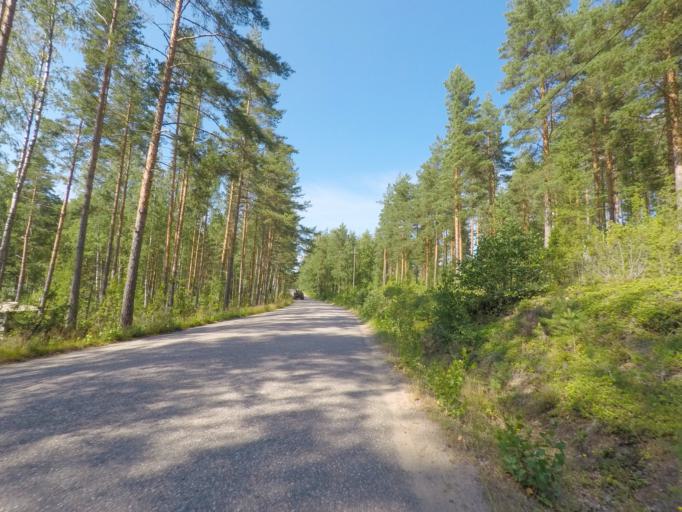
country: FI
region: Southern Savonia
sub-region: Mikkeli
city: Puumala
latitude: 61.4356
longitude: 28.1702
